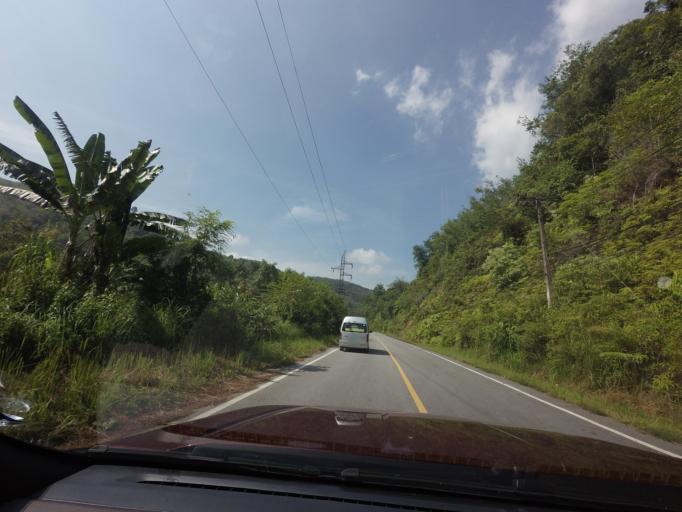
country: TH
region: Yala
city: Betong
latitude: 5.9309
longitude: 101.1861
